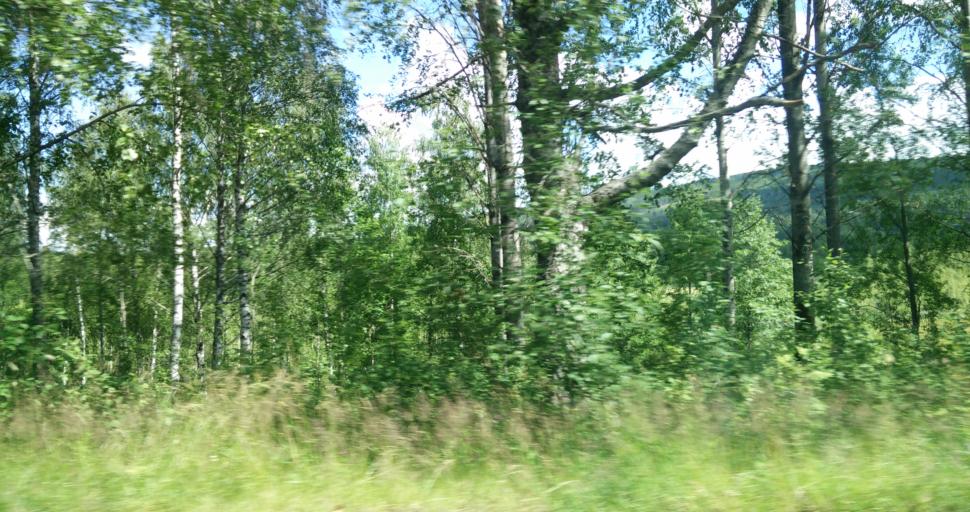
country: SE
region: Vaermland
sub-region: Hagfors Kommun
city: Hagfors
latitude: 60.0230
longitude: 13.6809
